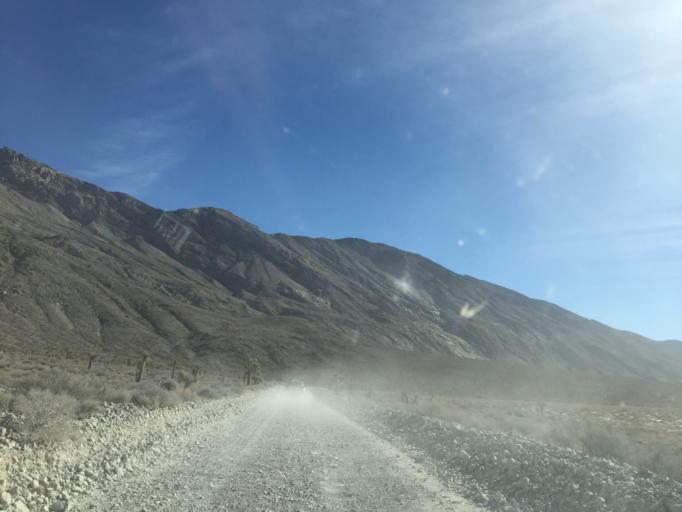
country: US
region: California
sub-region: Inyo County
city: Lone Pine
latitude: 36.8538
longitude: -117.4995
